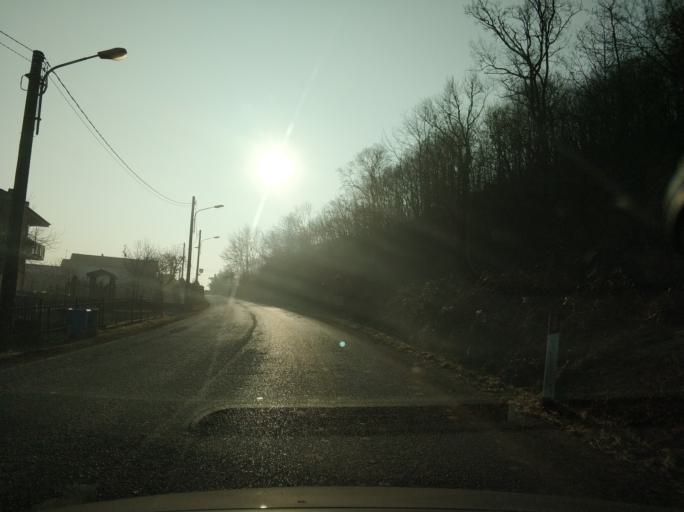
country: IT
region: Piedmont
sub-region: Provincia di Torino
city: Rivarossa
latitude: 45.2536
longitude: 7.7113
